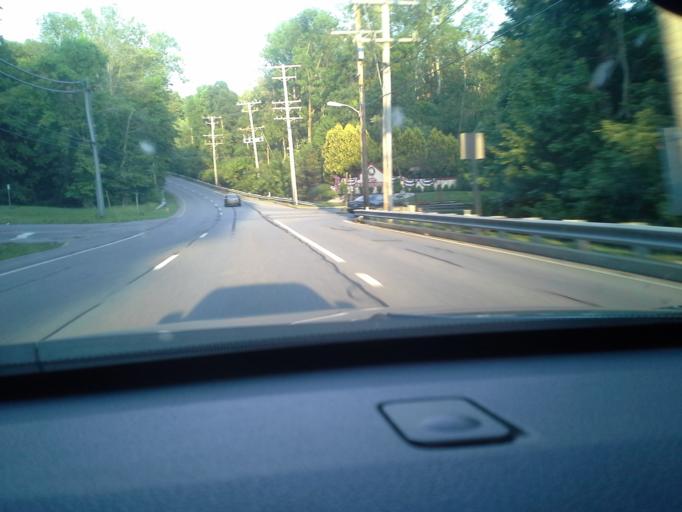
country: US
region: Maryland
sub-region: Calvert County
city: Chesapeake Beach
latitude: 38.6997
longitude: -76.5574
